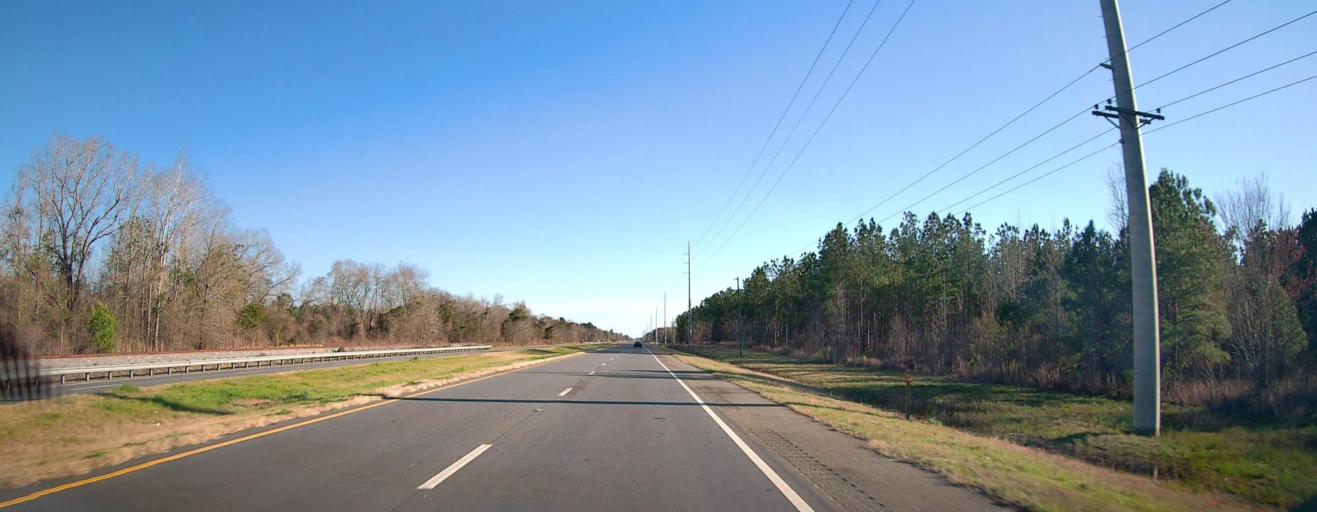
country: US
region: Georgia
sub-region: Lee County
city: Leesburg
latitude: 31.8640
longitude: -84.2348
